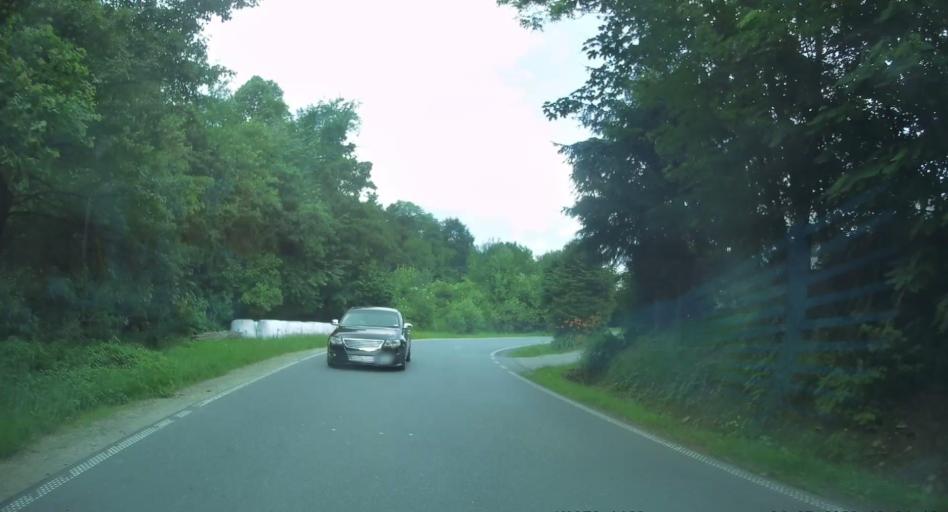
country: PL
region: Lesser Poland Voivodeship
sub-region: Powiat nowosadecki
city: Korzenna
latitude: 49.7211
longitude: 20.7742
